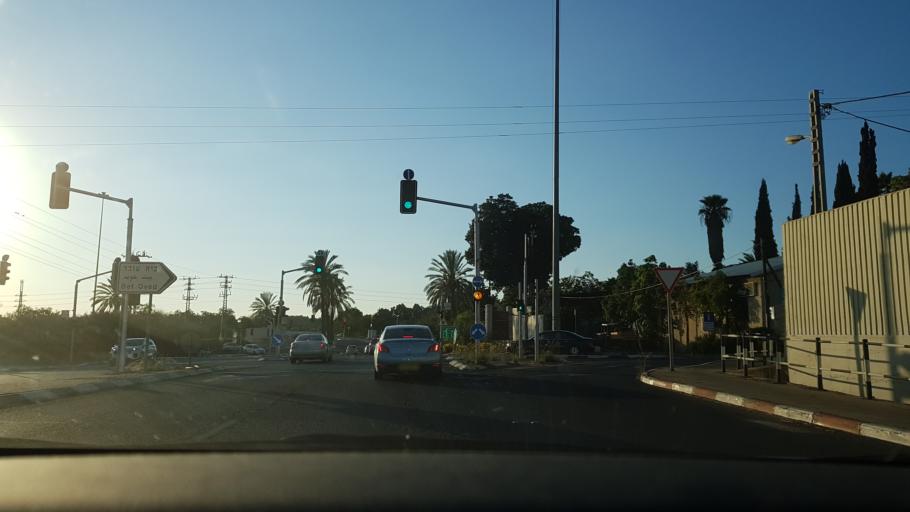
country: IL
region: Central District
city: Ness Ziona
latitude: 31.9204
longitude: 34.7721
